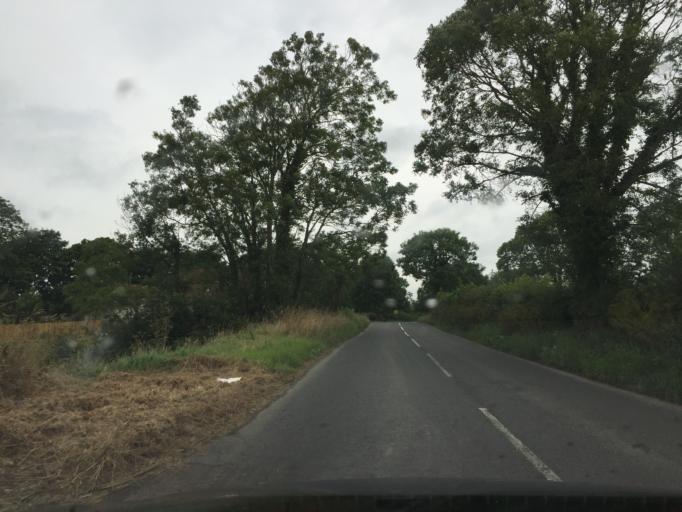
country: GB
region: Northern Ireland
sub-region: Down District
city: Kircubbin
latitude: 54.4922
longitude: -5.4983
